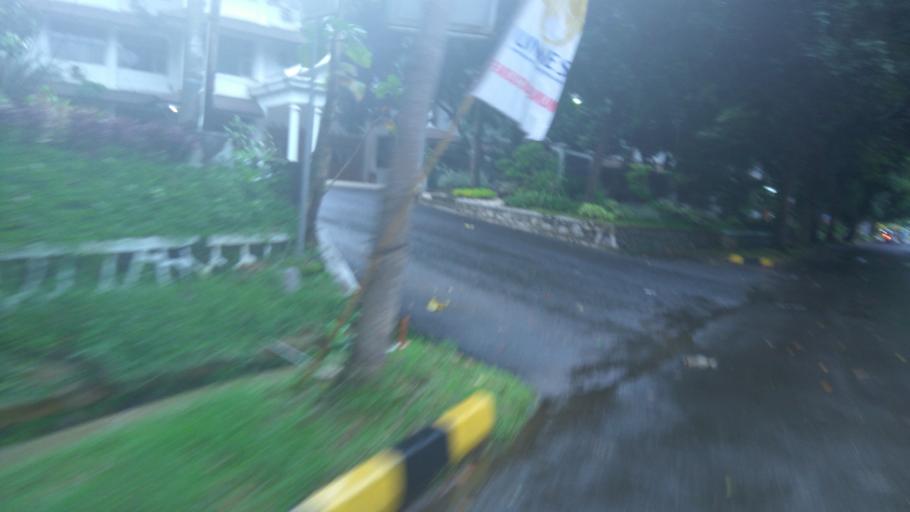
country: ID
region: Central Java
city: Semarang
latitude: -7.0499
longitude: 110.3979
